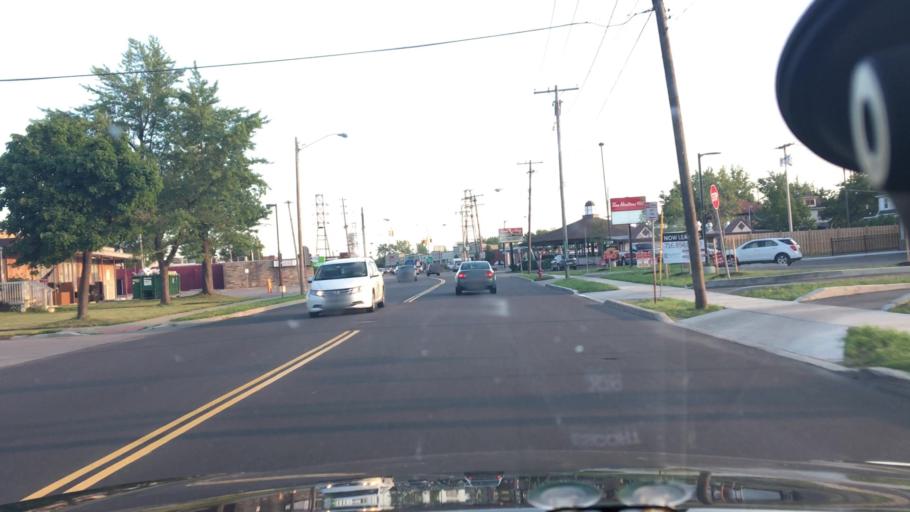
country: US
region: New York
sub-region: Erie County
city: Tonawanda
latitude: 43.0028
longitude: -78.8750
